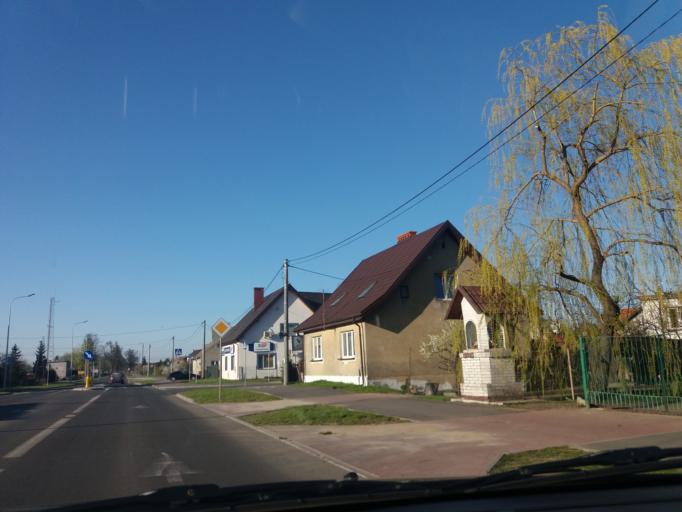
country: PL
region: Warmian-Masurian Voivodeship
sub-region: Powiat nidzicki
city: Nidzica
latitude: 53.3726
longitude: 20.4290
